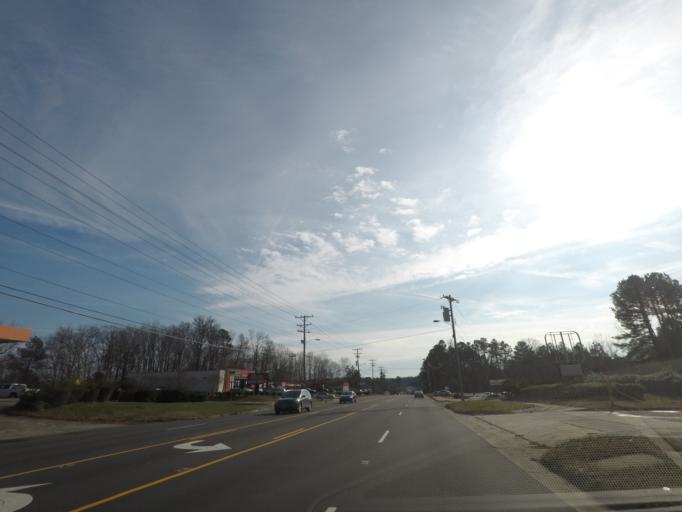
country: US
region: North Carolina
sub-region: Durham County
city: Durham
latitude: 36.0761
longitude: -78.9098
